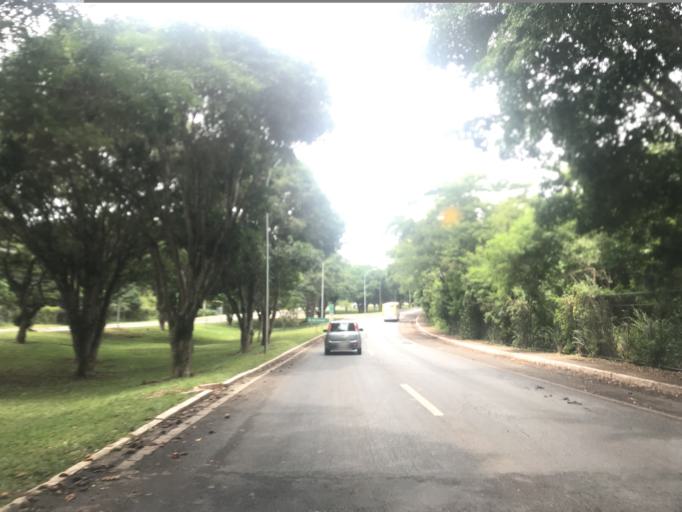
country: BR
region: Federal District
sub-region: Brasilia
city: Brasilia
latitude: -15.8404
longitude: -47.8392
